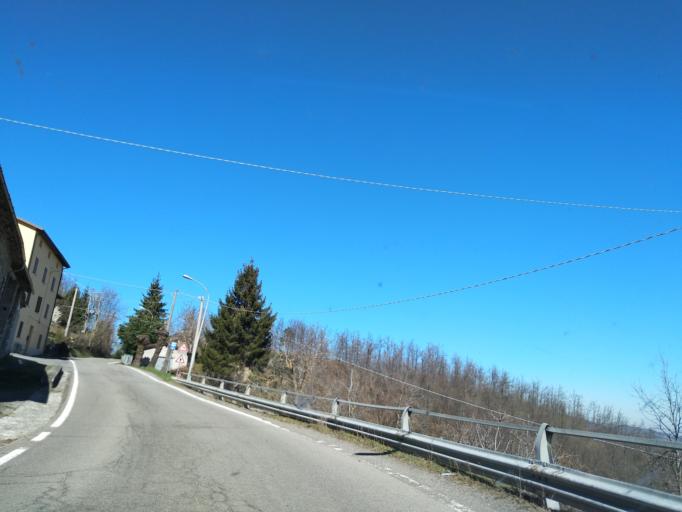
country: IT
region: Emilia-Romagna
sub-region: Provincia di Reggio Emilia
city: Ramiseto
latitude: 44.4149
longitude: 10.2985
